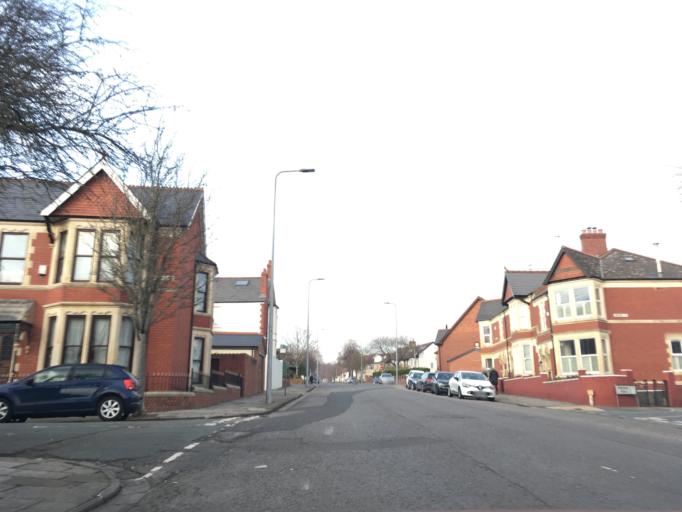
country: GB
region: Wales
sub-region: Cardiff
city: Cardiff
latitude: 51.4965
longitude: -3.1566
